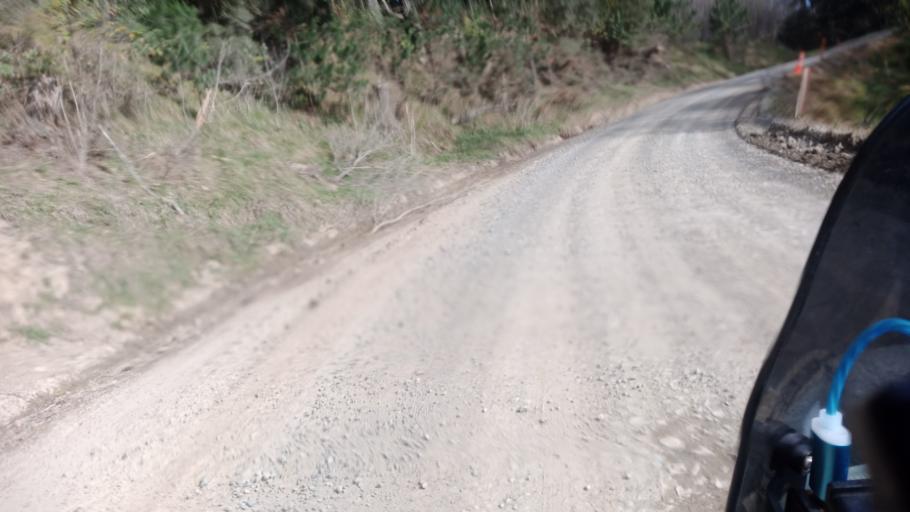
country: NZ
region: Gisborne
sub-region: Gisborne District
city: Gisborne
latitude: -38.1406
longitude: 178.1912
